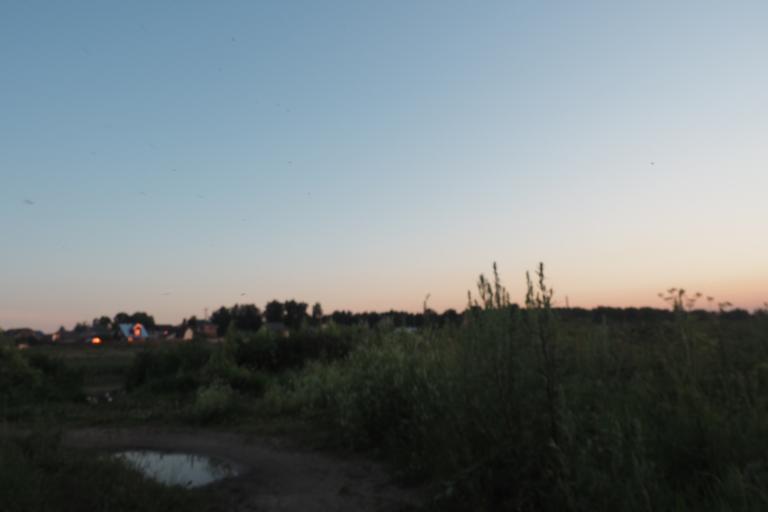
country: RU
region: Moskovskaya
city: Malyshevo
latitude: 55.5524
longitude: 38.3182
